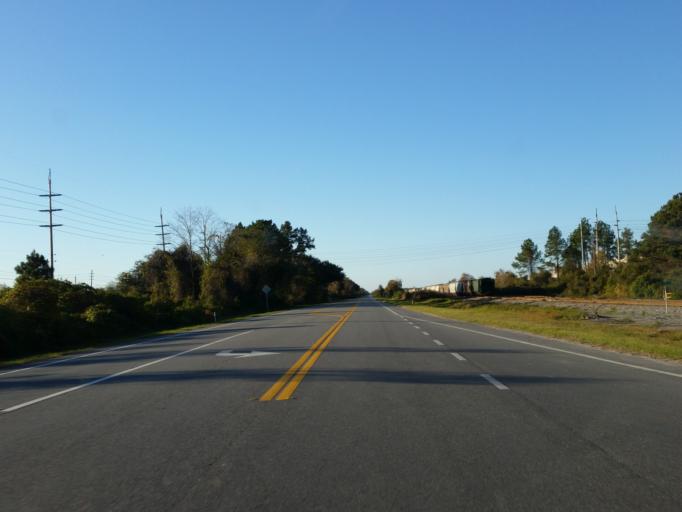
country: US
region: Florida
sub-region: Hamilton County
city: Jasper
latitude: 30.4362
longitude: -82.8719
